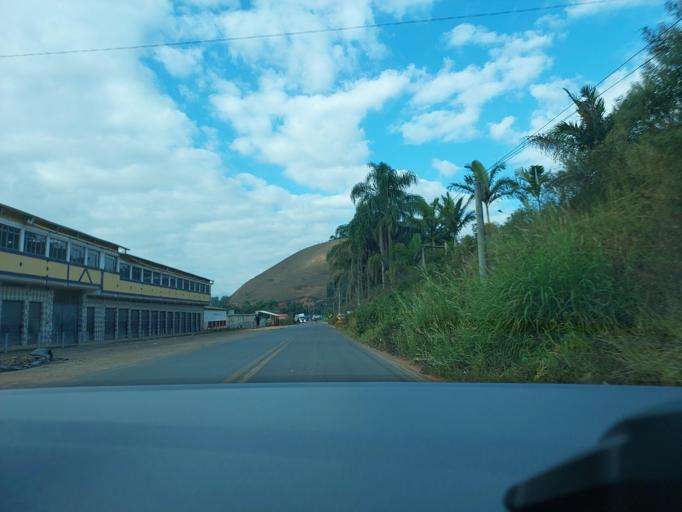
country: BR
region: Minas Gerais
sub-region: Vicosa
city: Vicosa
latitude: -20.8440
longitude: -42.6789
